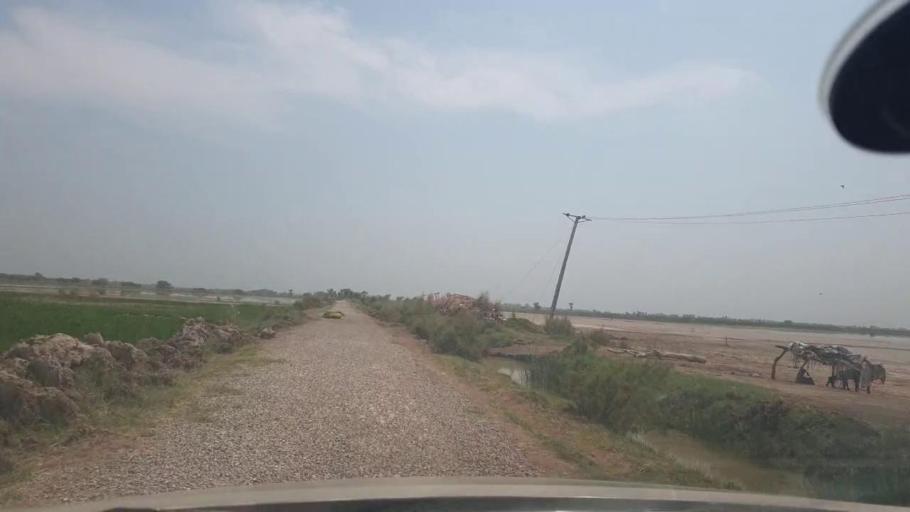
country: PK
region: Sindh
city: Jacobabad
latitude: 28.2300
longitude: 68.3922
